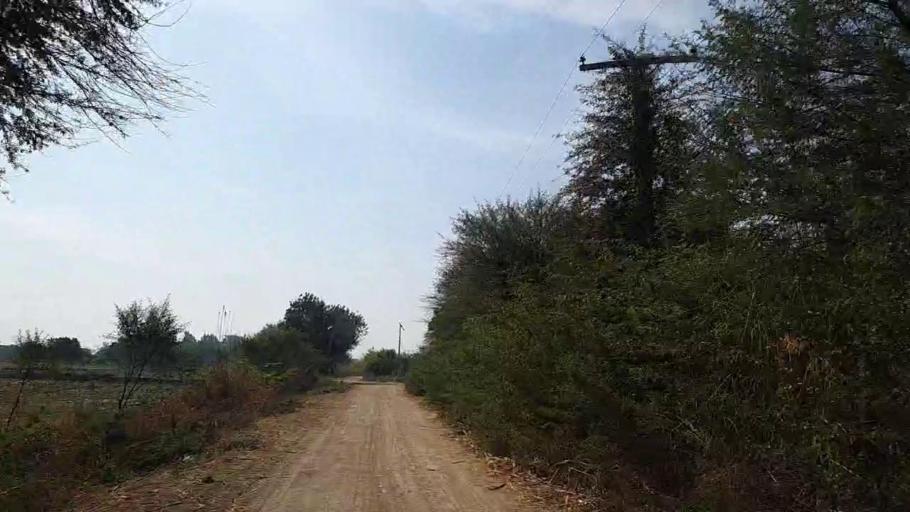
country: PK
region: Sindh
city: Mirpur Khas
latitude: 25.4737
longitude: 68.9745
